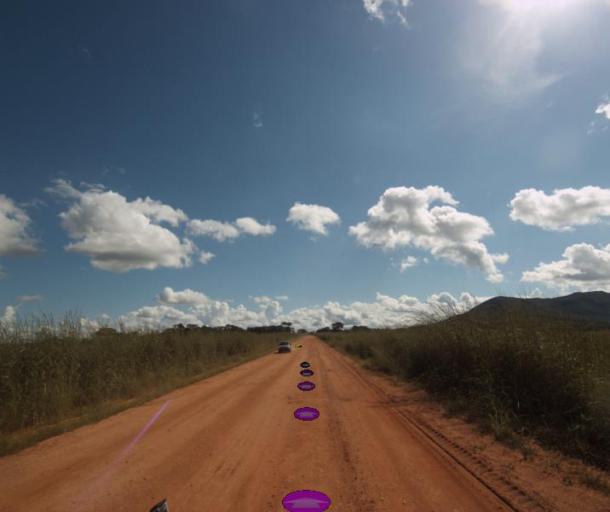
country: BR
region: Goias
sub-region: Jaragua
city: Jaragua
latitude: -15.8351
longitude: -49.2687
